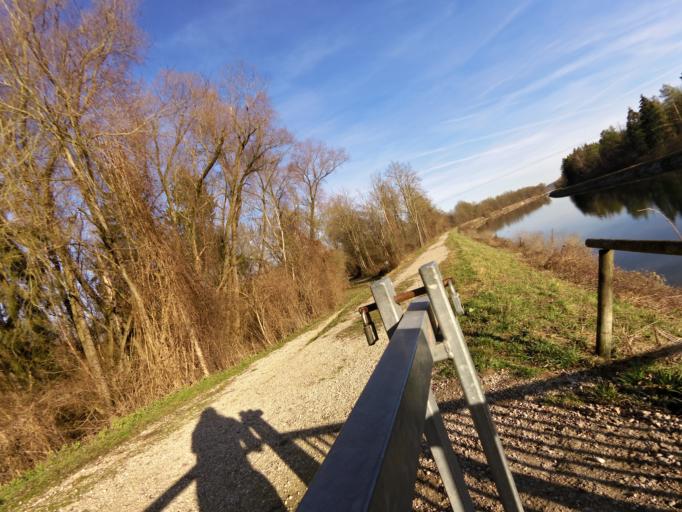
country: DE
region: Bavaria
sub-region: Lower Bavaria
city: Bruckberg
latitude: 48.4992
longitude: 12.0178
